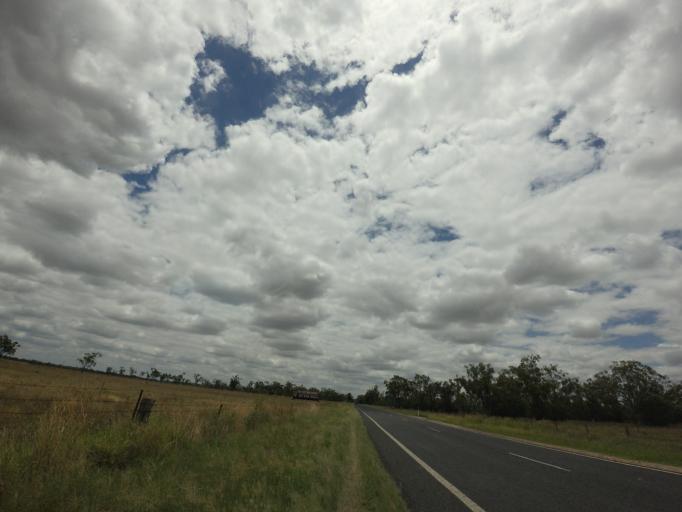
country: AU
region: Queensland
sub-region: Goondiwindi
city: Goondiwindi
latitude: -28.5016
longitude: 150.2913
